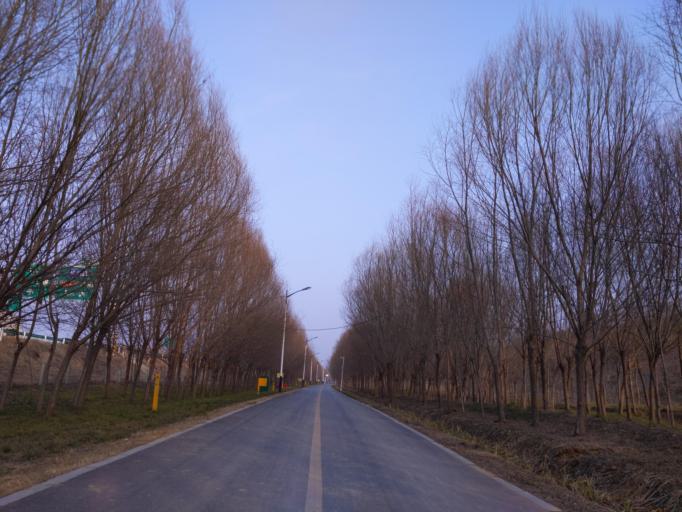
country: CN
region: Henan Sheng
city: Puyang
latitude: 35.8211
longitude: 115.0077
